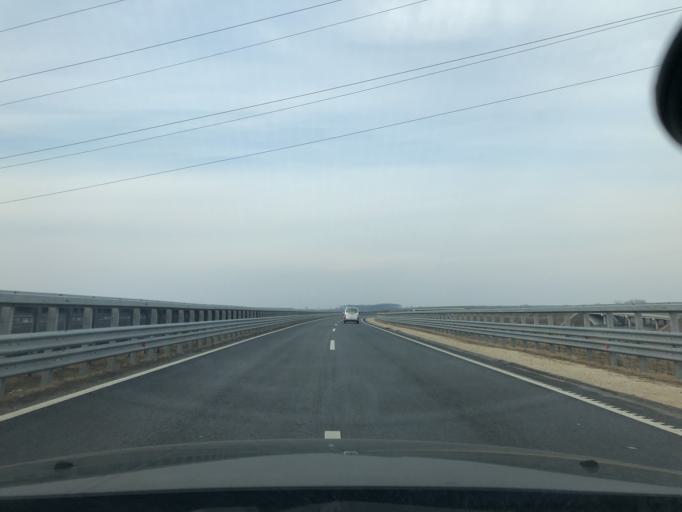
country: HU
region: Gyor-Moson-Sopron
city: Csorna
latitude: 47.6137
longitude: 17.2785
